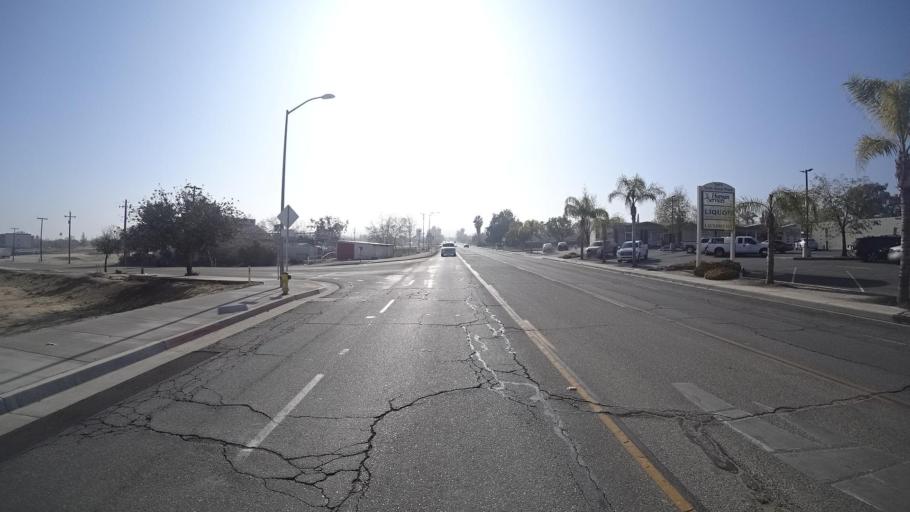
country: US
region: California
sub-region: Kern County
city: Taft
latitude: 35.1421
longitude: -119.4651
